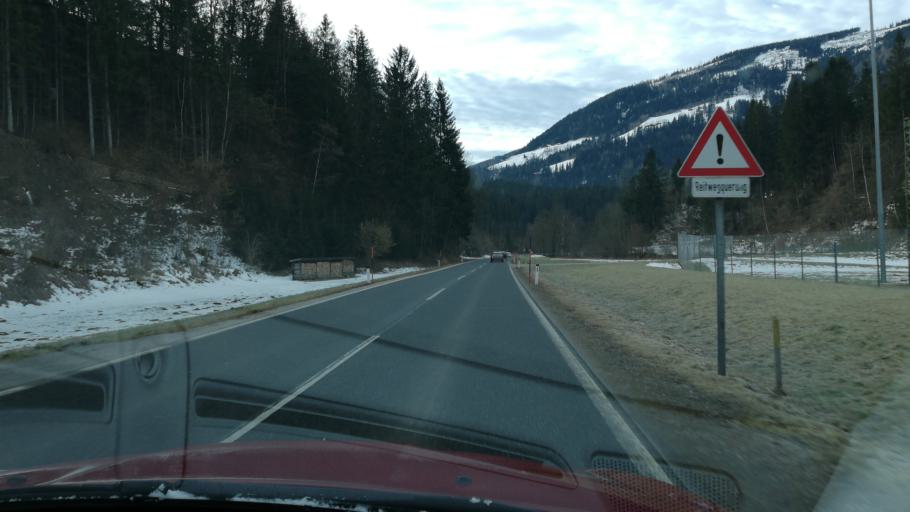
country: AT
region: Styria
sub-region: Politischer Bezirk Liezen
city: Irdning
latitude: 47.4906
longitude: 14.1078
